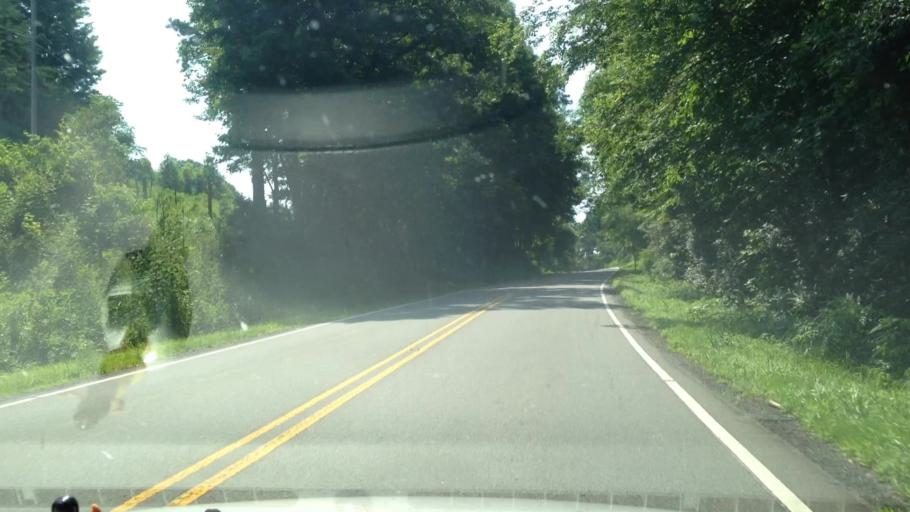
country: US
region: North Carolina
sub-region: Surry County
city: Flat Rock
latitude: 36.5365
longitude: -80.5151
